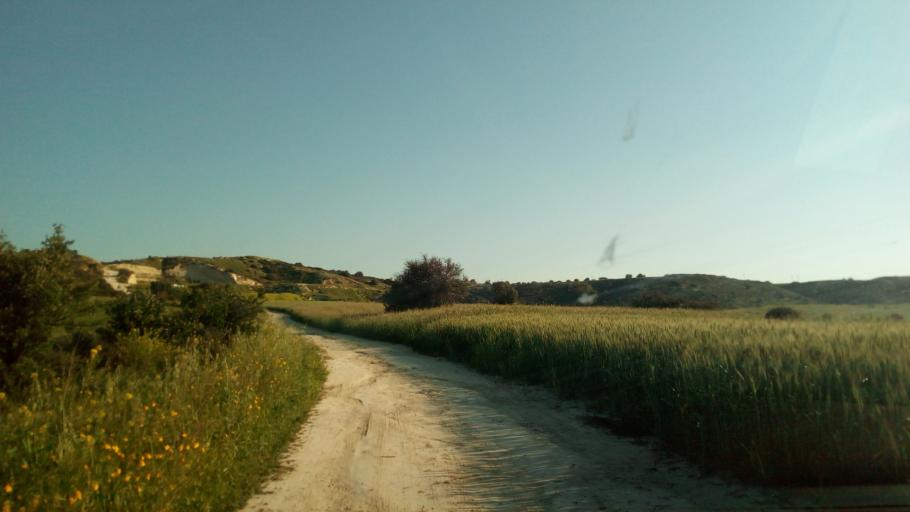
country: CY
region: Larnaka
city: Kofinou
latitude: 34.8407
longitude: 33.4485
